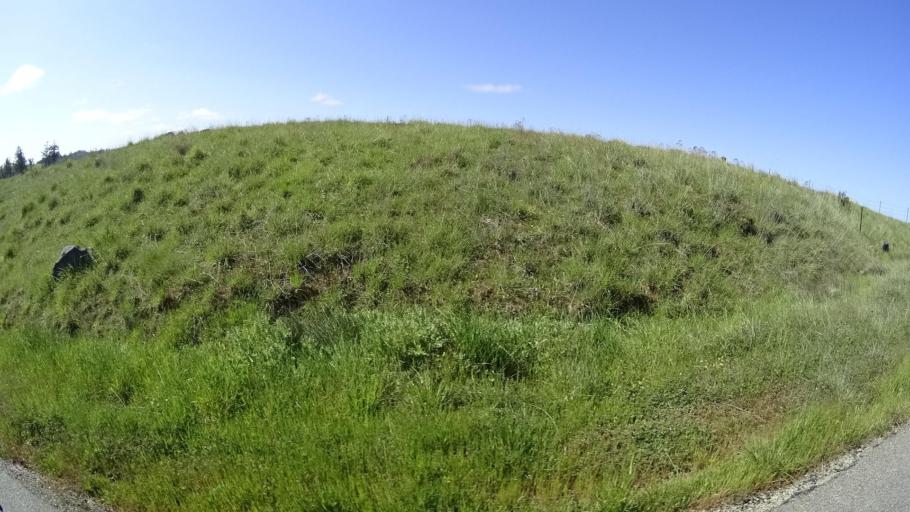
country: US
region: California
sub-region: Humboldt County
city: Redway
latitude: 40.0878
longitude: -123.6750
